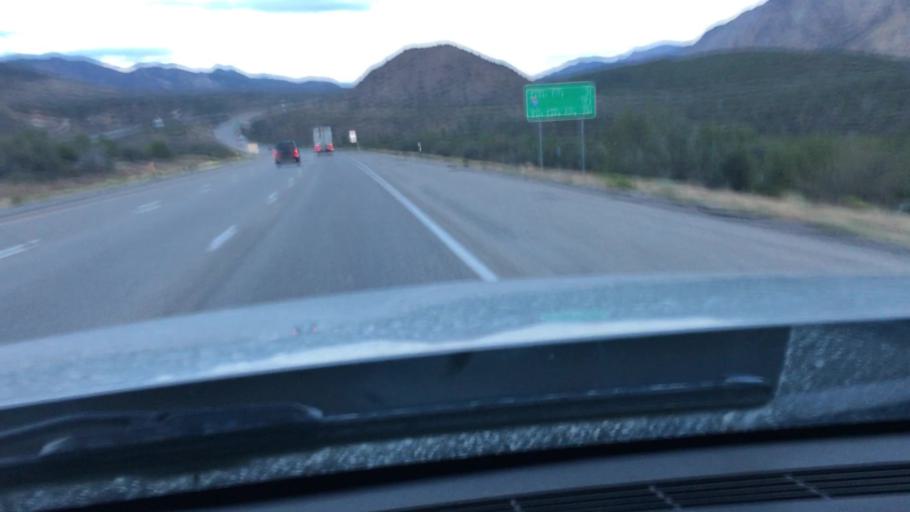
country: US
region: Utah
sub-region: Washington County
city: Toquerville
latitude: 37.2970
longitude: -113.2986
